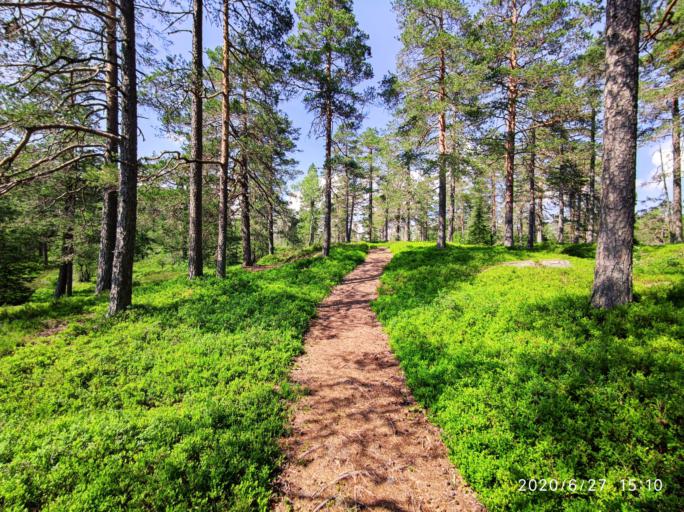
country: NO
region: Buskerud
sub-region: Kongsberg
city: Kongsberg
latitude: 59.6648
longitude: 9.5867
